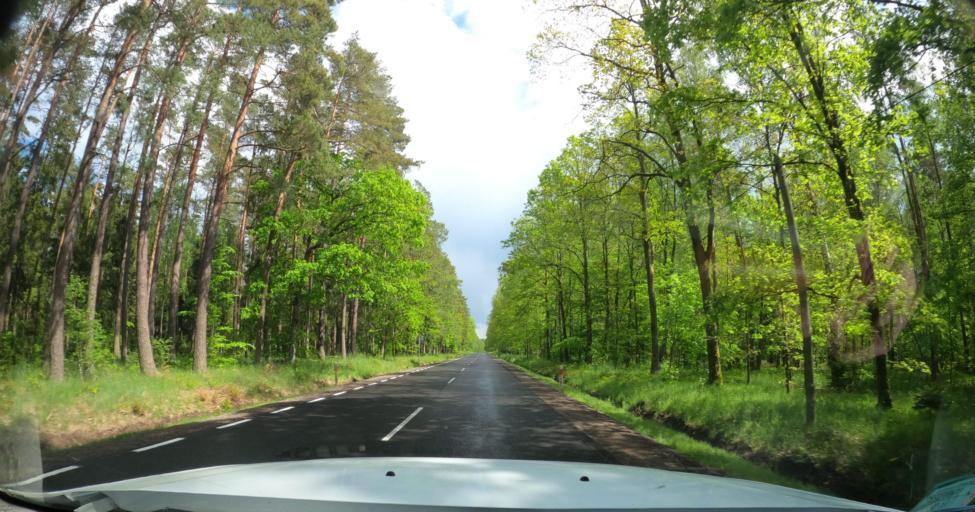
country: PL
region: Pomeranian Voivodeship
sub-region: Powiat bytowski
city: Czarna Dabrowka
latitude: 54.3428
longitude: 17.6023
